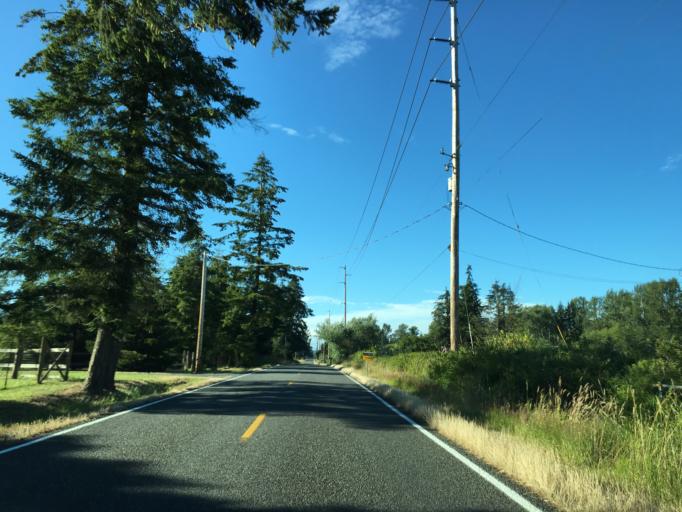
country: US
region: Washington
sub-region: Whatcom County
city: Birch Bay
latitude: 48.9283
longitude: -122.7044
